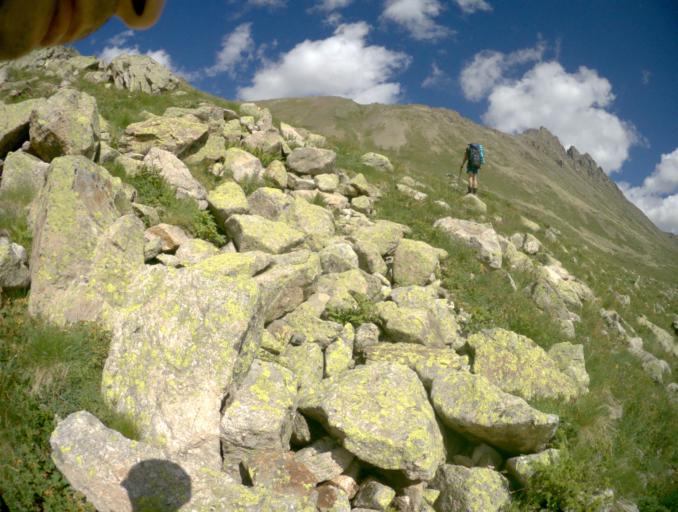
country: RU
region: Karachayevo-Cherkesiya
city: Uchkulan
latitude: 43.3256
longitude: 42.0983
